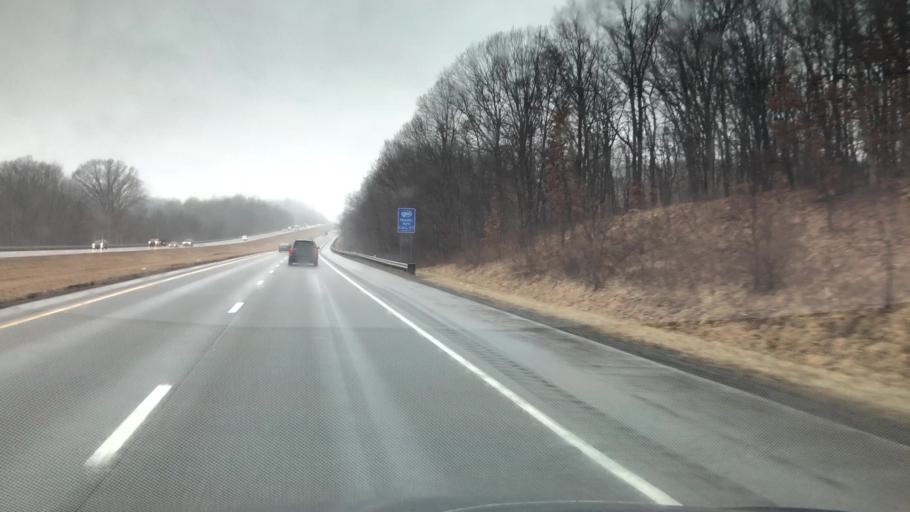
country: US
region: Ohio
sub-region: Muskingum County
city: Zanesville
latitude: 39.9474
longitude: -82.1489
